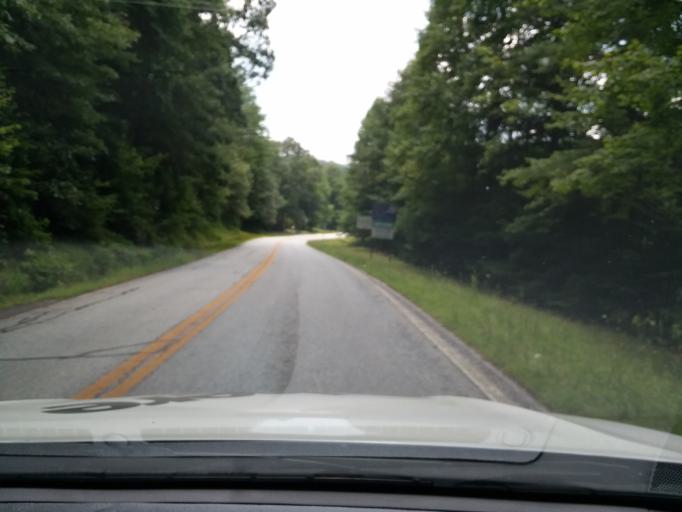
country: US
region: Georgia
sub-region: Rabun County
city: Mountain City
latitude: 34.9981
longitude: -83.1975
